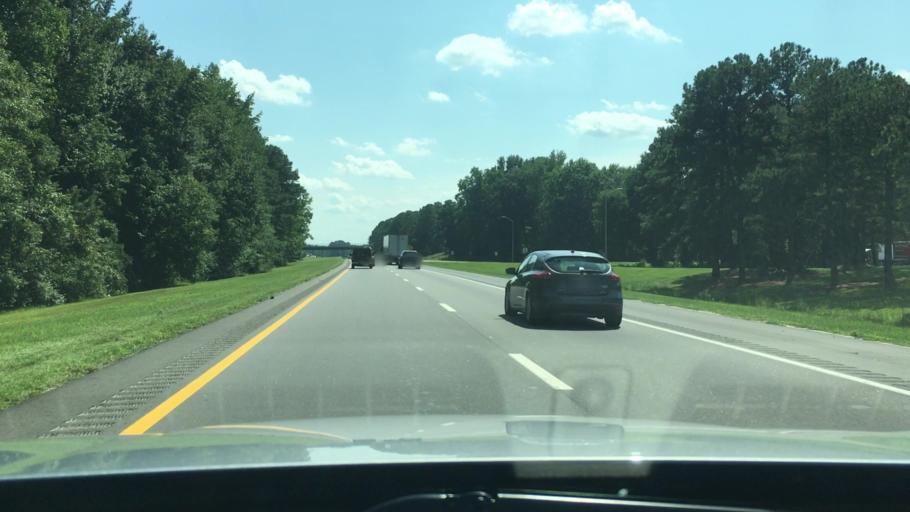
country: US
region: North Carolina
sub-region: Cumberland County
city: Vander
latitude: 34.9946
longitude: -78.8332
